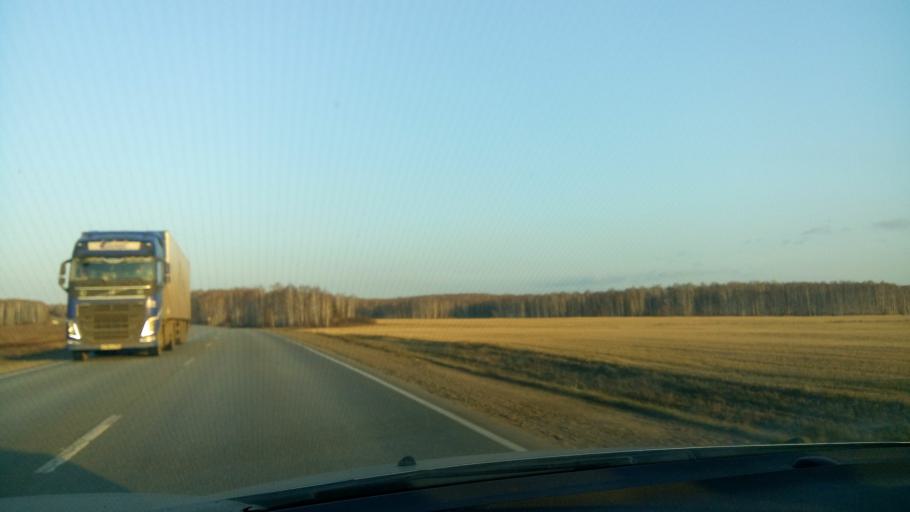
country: RU
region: Sverdlovsk
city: Yelanskiy
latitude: 56.7596
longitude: 62.3915
